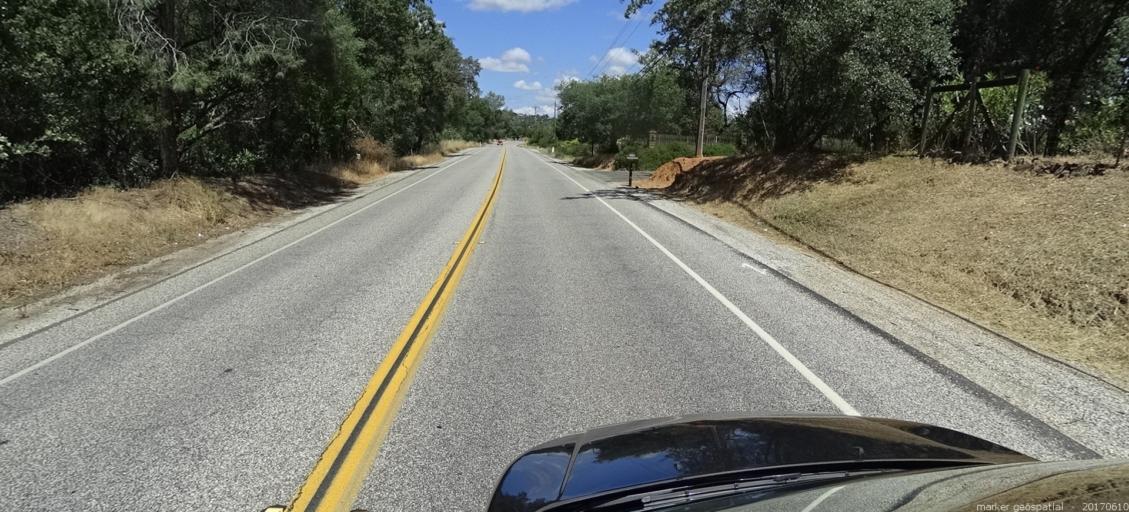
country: US
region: California
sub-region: Butte County
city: Oroville East
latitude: 39.5005
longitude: -121.4583
